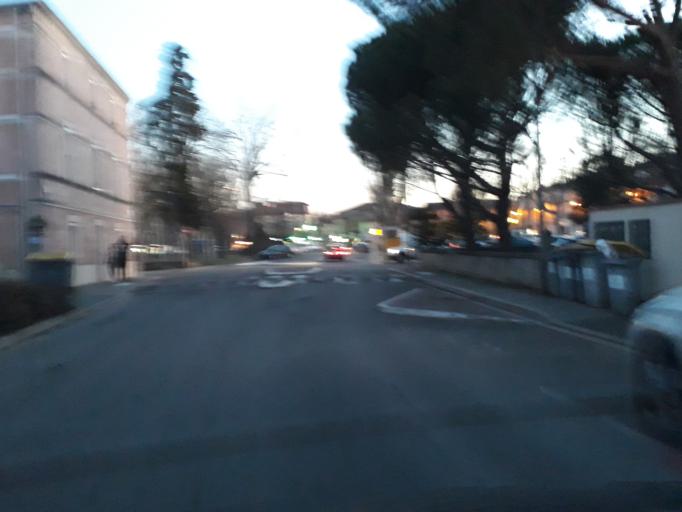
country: FR
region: Midi-Pyrenees
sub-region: Departement de la Haute-Garonne
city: Carbonne
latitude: 43.2974
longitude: 1.2253
